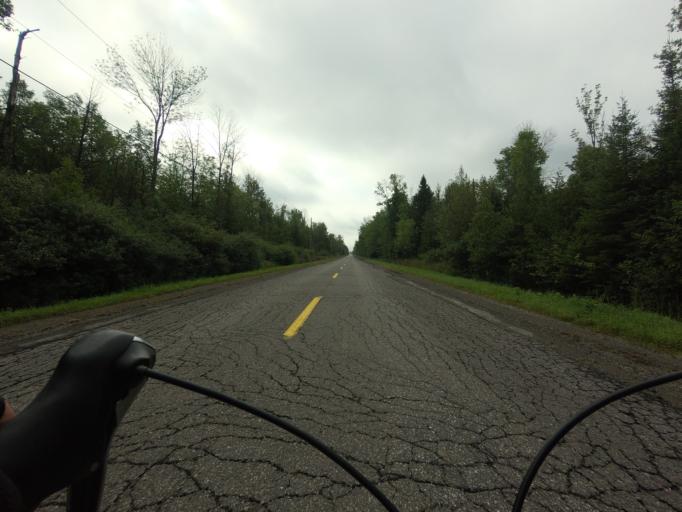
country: CA
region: Ontario
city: Bells Corners
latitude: 45.0636
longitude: -75.7224
